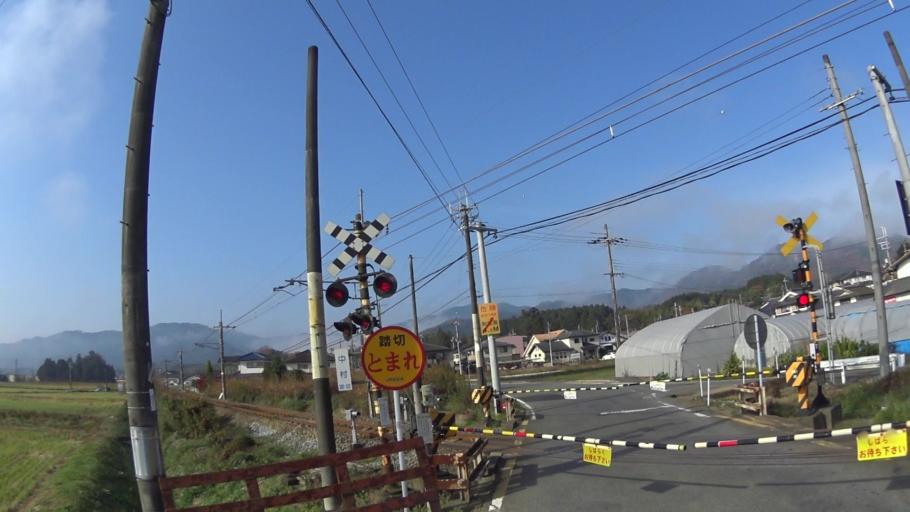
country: JP
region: Kyoto
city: Fukuchiyama
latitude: 35.2482
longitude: 135.1436
